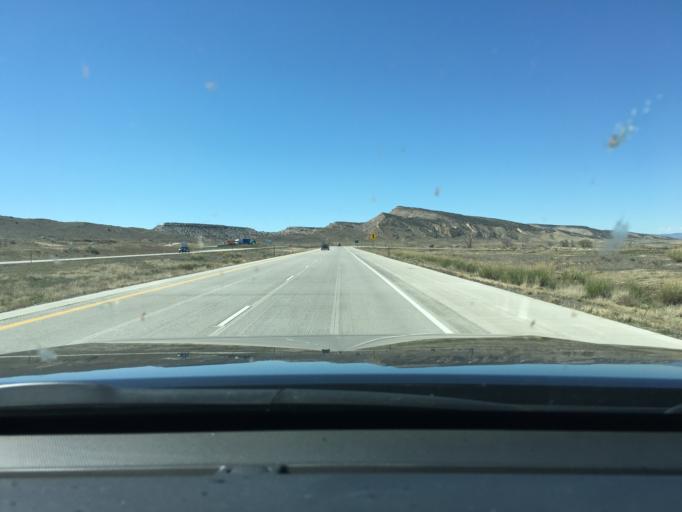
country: US
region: Colorado
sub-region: Mesa County
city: Loma
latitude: 39.1784
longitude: -108.8139
